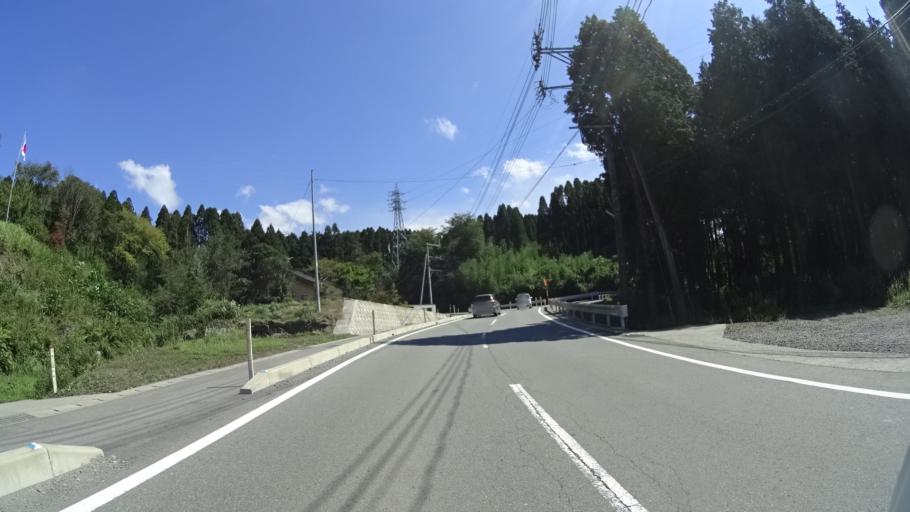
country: JP
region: Kumamoto
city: Aso
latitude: 32.8841
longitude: 130.9973
